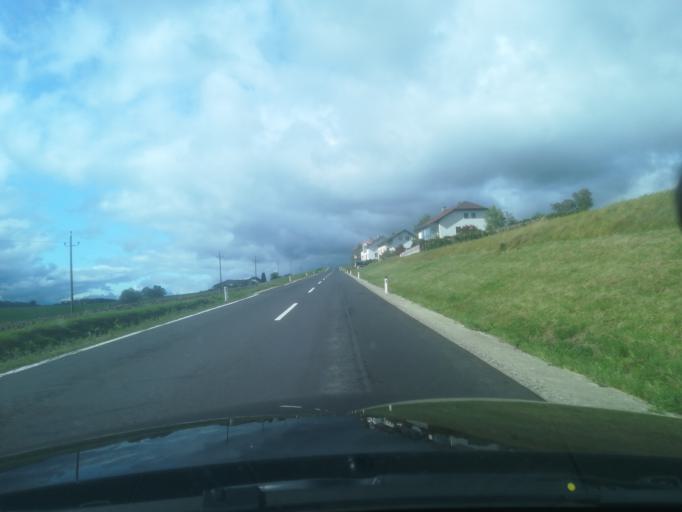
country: AT
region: Upper Austria
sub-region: Politischer Bezirk Urfahr-Umgebung
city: Gramastetten
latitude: 48.3933
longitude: 14.1843
